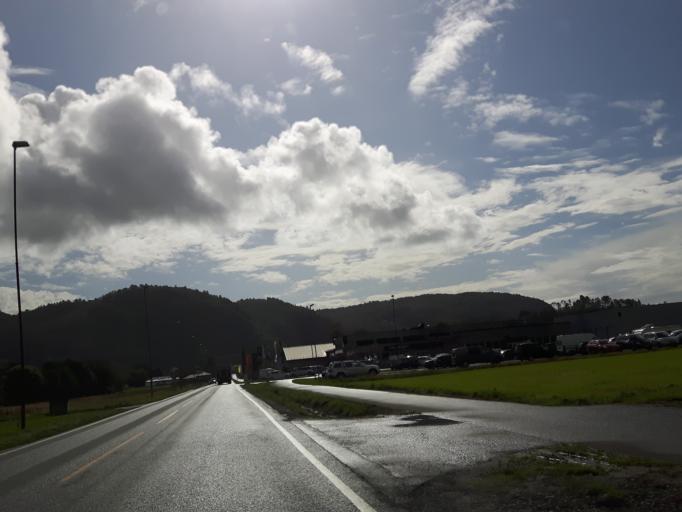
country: NO
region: Vest-Agder
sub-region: Lyngdal
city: Lyngdal
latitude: 58.1435
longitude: 7.0600
